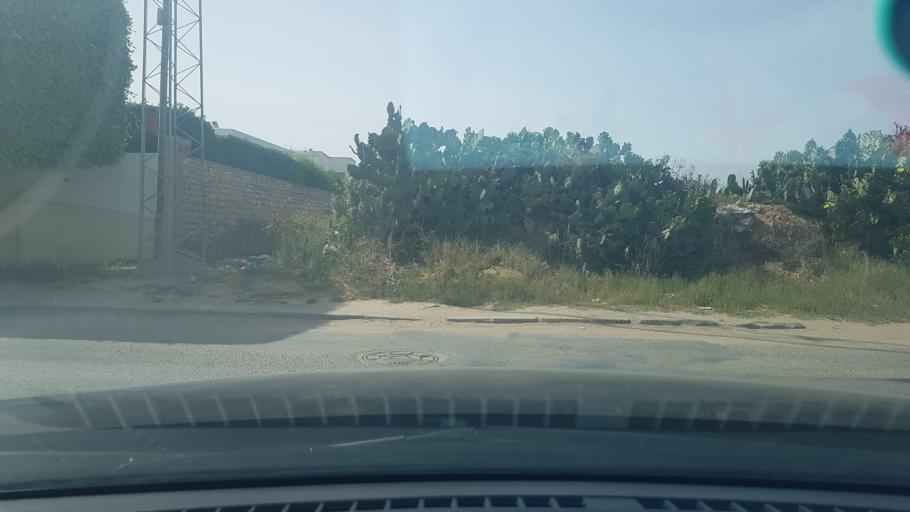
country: TN
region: Safaqis
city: Al Qarmadah
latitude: 34.8070
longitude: 10.7664
